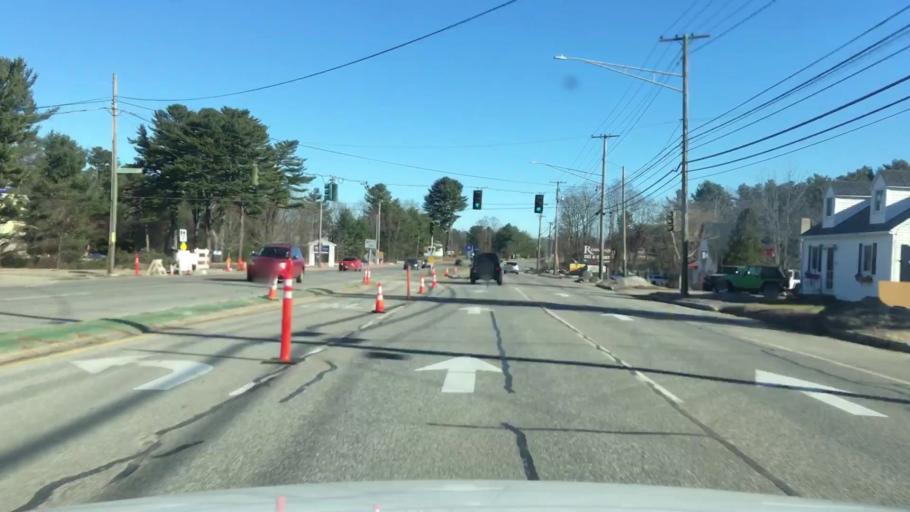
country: US
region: Maine
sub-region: Cumberland County
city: Scarborough
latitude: 43.5870
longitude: -70.3518
